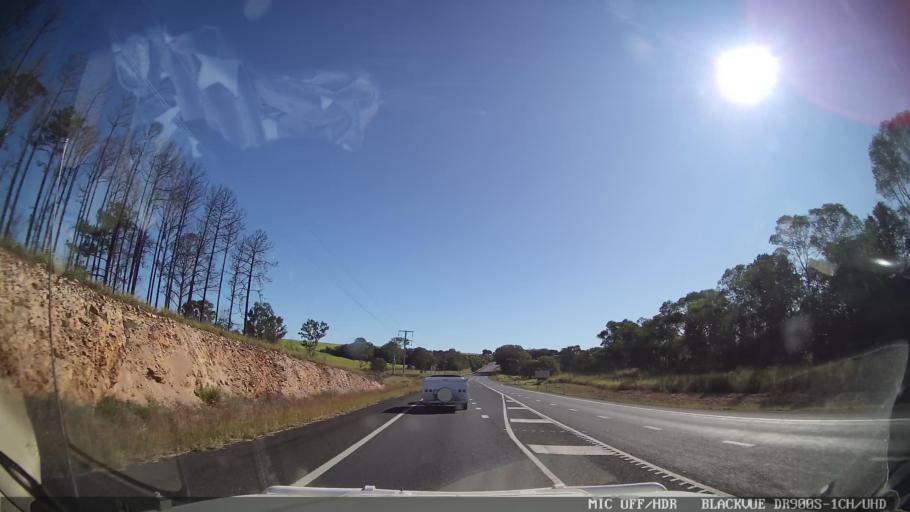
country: AU
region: Queensland
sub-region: Bundaberg
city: Childers
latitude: -25.2470
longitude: 152.3217
